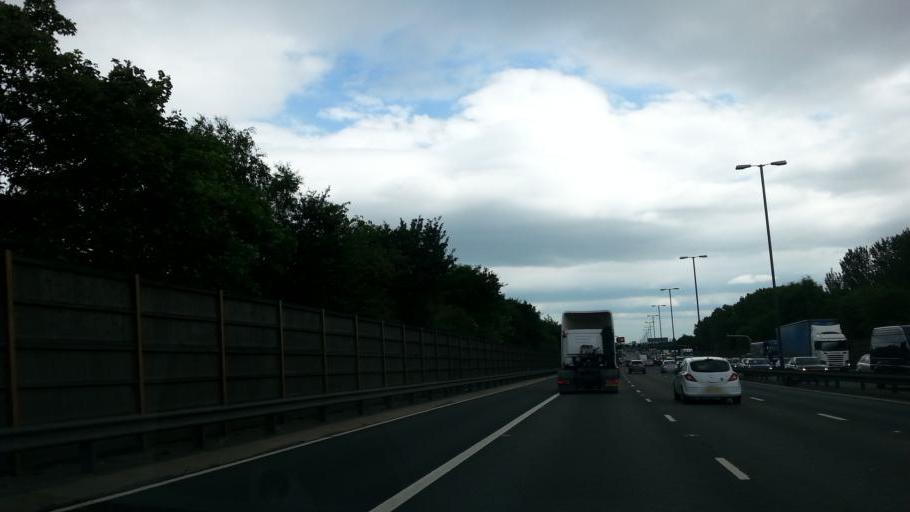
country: GB
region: England
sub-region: City and Borough of Birmingham
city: Hockley
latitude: 52.5457
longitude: -1.9174
